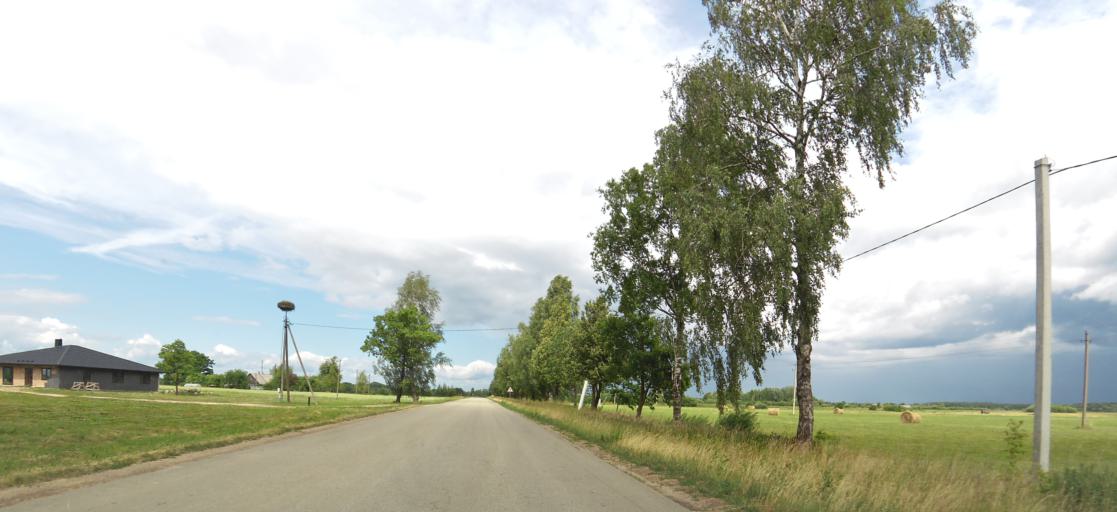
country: LT
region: Panevezys
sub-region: Birzai
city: Birzai
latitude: 56.3823
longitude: 24.7739
